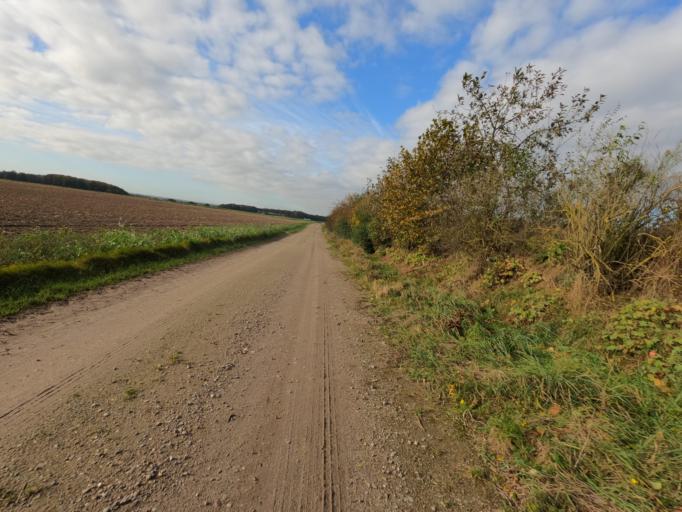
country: DE
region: North Rhine-Westphalia
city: Huckelhoven
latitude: 51.0495
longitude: 6.2703
